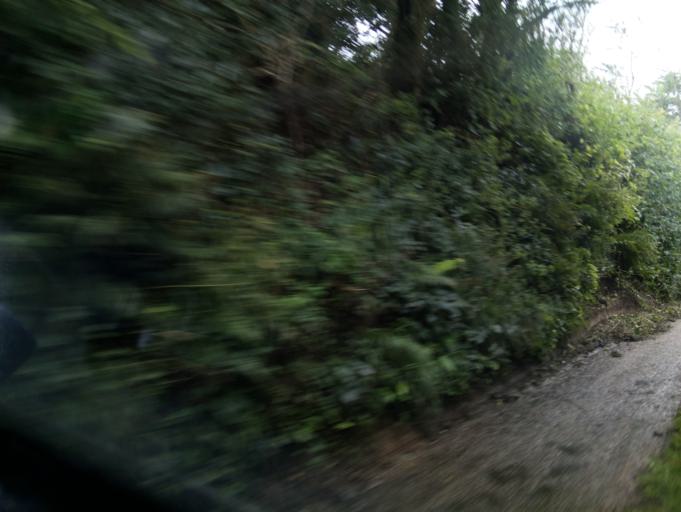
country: GB
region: England
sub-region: Devon
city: Kingsbridge
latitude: 50.2729
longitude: -3.8249
